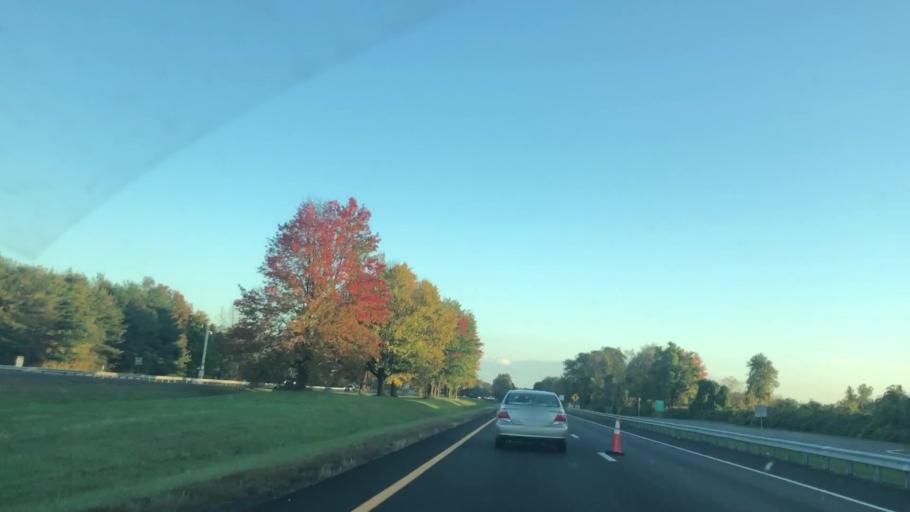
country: US
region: Massachusetts
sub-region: Franklin County
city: South Deerfield
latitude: 42.5061
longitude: -72.6207
